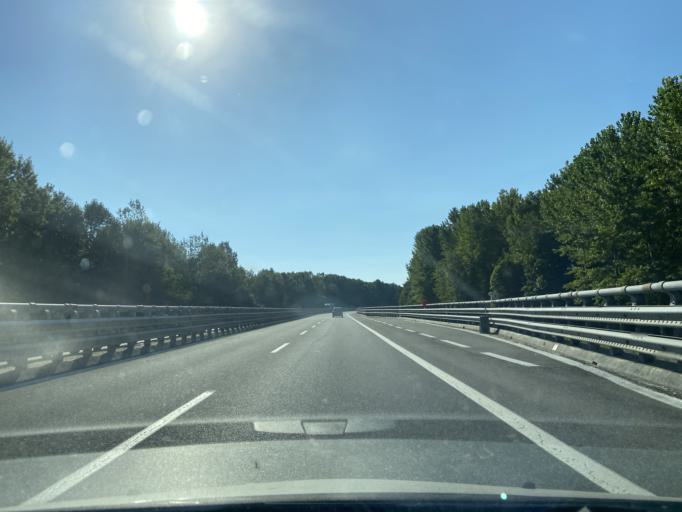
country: IT
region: Piedmont
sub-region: Provincia di Torino
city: Sant'Ambrogio di Torino
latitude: 45.1099
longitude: 7.3608
